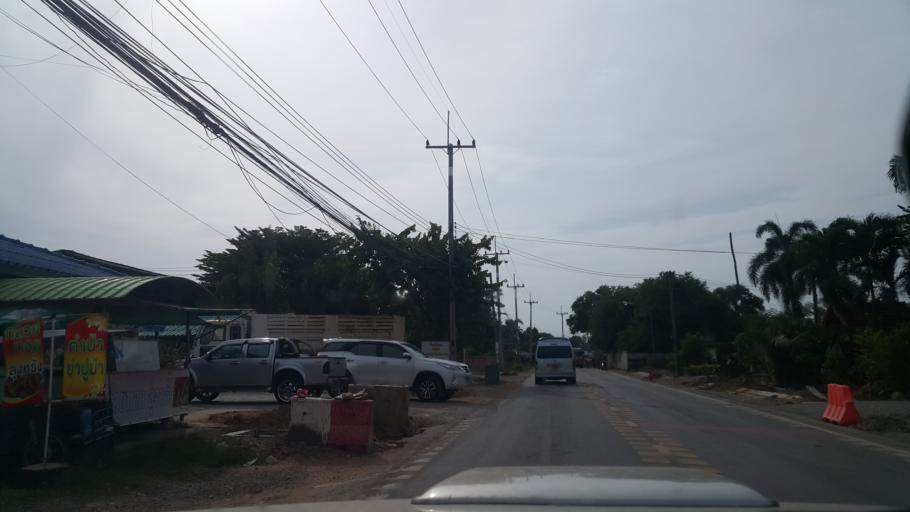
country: TH
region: Chon Buri
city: Sattahip
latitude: 12.7880
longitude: 100.9309
